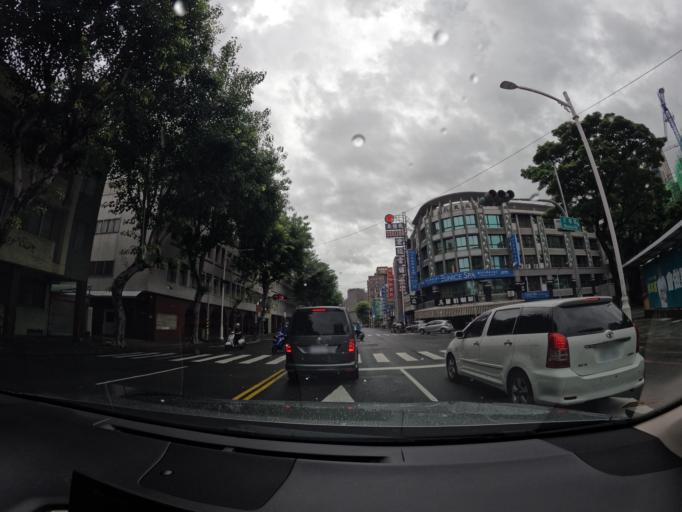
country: TW
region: Kaohsiung
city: Kaohsiung
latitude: 22.6335
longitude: 120.3212
